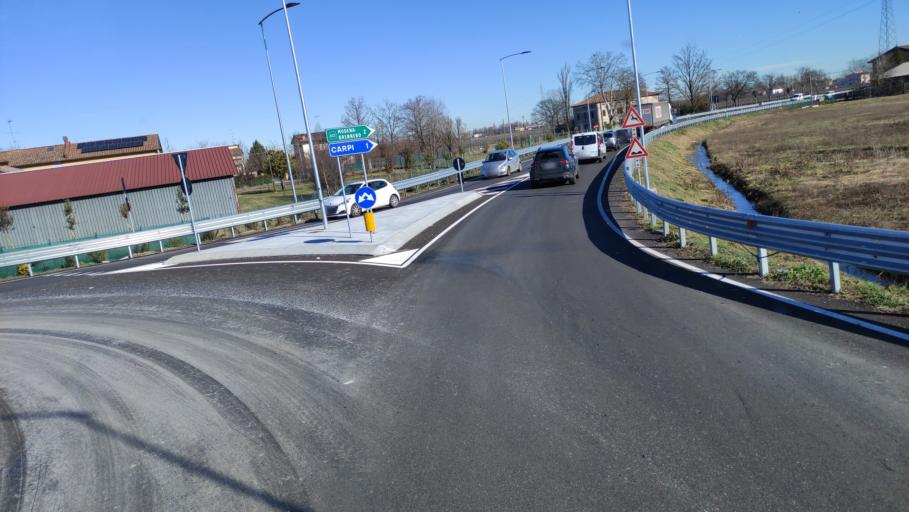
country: IT
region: Emilia-Romagna
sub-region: Provincia di Modena
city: Santa Croce Scuole
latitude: 44.7674
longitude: 10.8310
